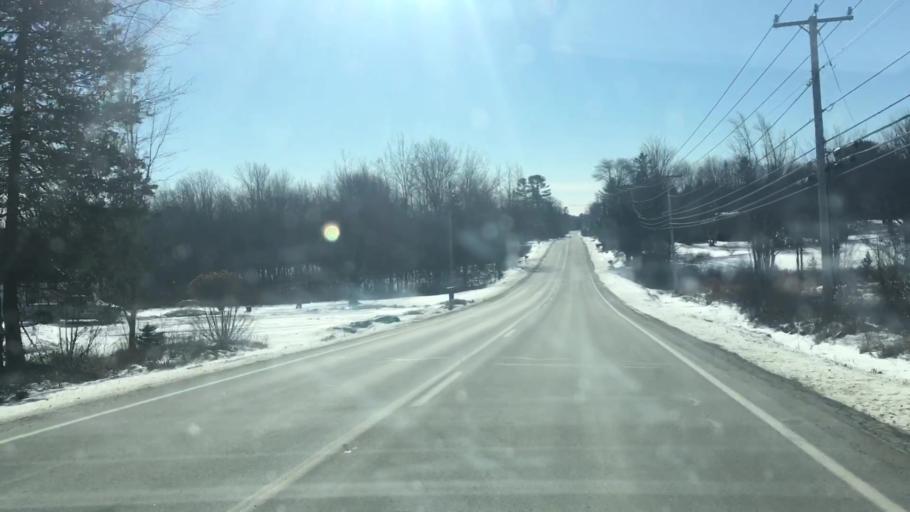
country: US
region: Maine
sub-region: Hancock County
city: Ellsworth
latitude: 44.5073
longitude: -68.4393
